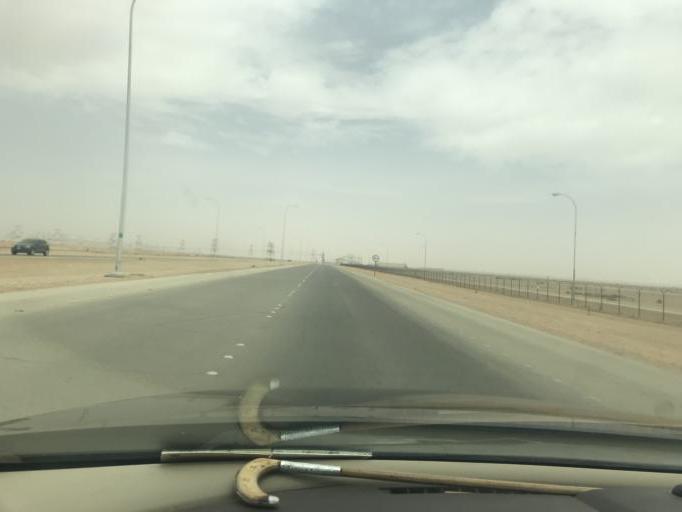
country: SA
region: Ar Riyad
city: Riyadh
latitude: 24.9679
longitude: 46.6651
